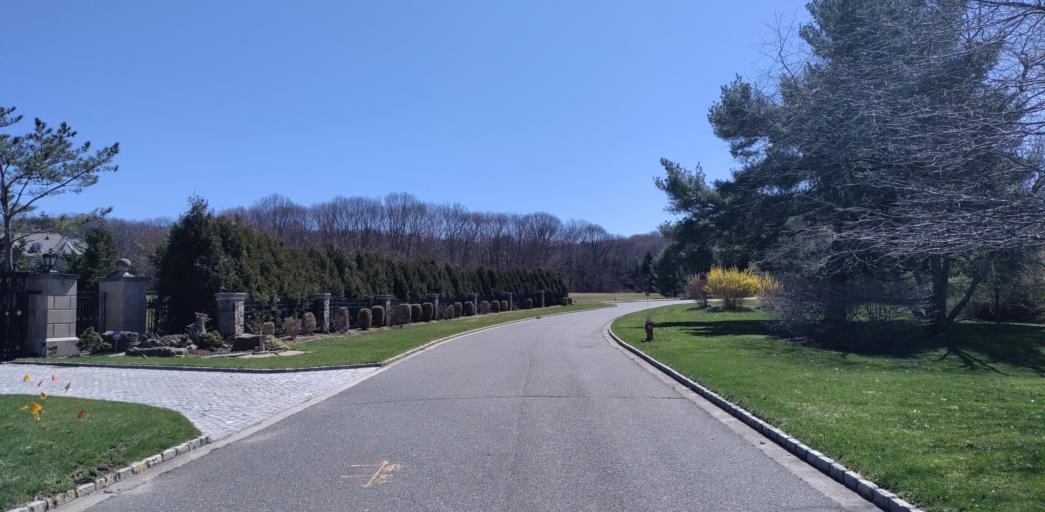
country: US
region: New York
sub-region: Nassau County
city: Greenvale
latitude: 40.8110
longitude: -73.6139
